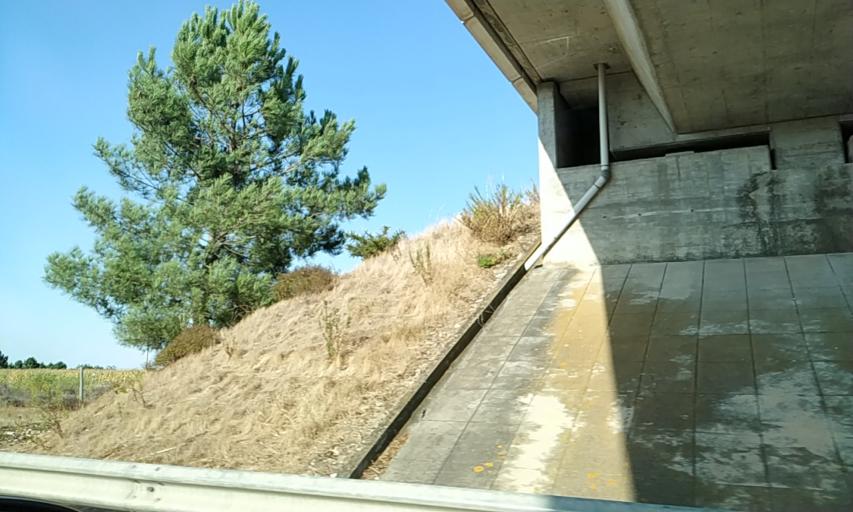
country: PT
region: Santarem
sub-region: Almeirim
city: Almeirim
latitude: 39.1726
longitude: -8.6208
